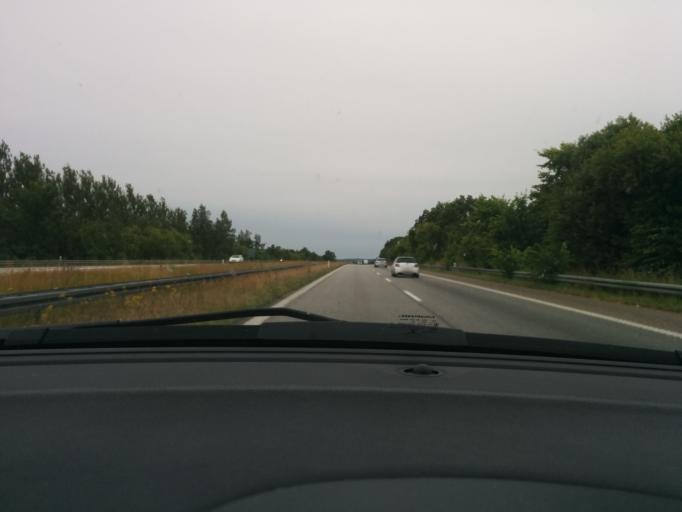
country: DK
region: Zealand
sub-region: Faxe Kommune
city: Ronnede
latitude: 55.3097
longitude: 12.0292
